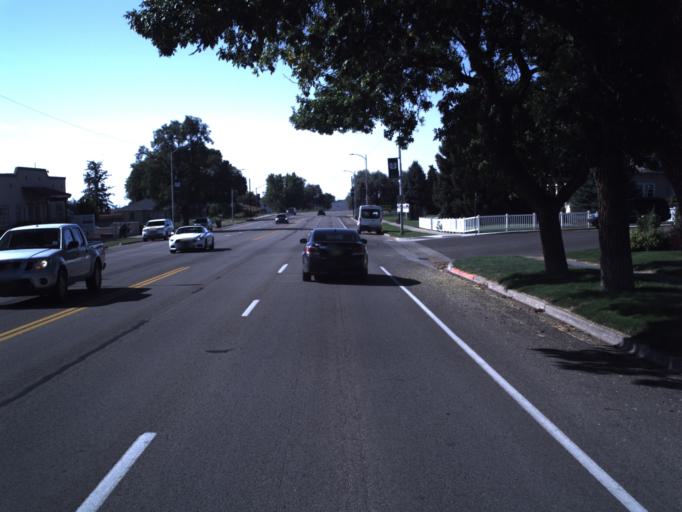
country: US
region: Utah
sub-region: San Juan County
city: Blanding
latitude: 37.6201
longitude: -109.4781
